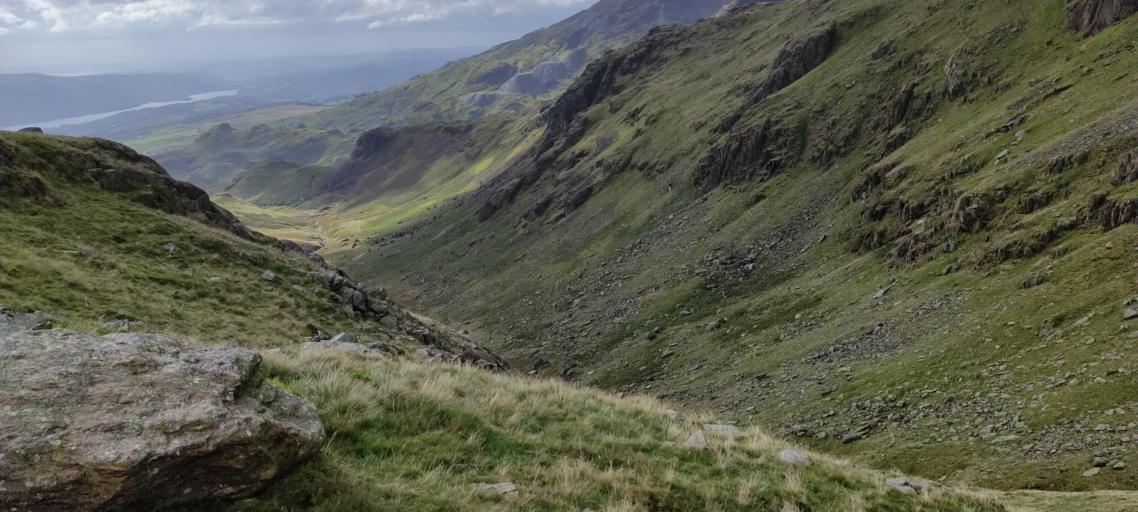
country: GB
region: England
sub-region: Cumbria
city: Ambleside
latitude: 54.3943
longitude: -3.1011
